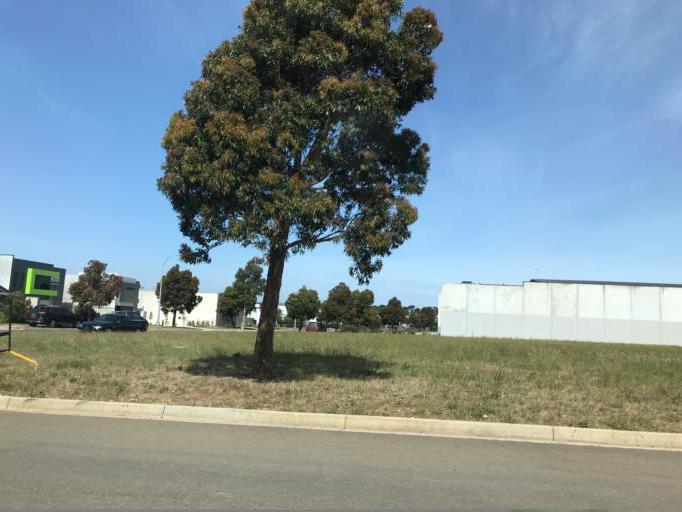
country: AU
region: Victoria
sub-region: Ballarat North
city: Newington
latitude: -37.5425
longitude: 143.7921
